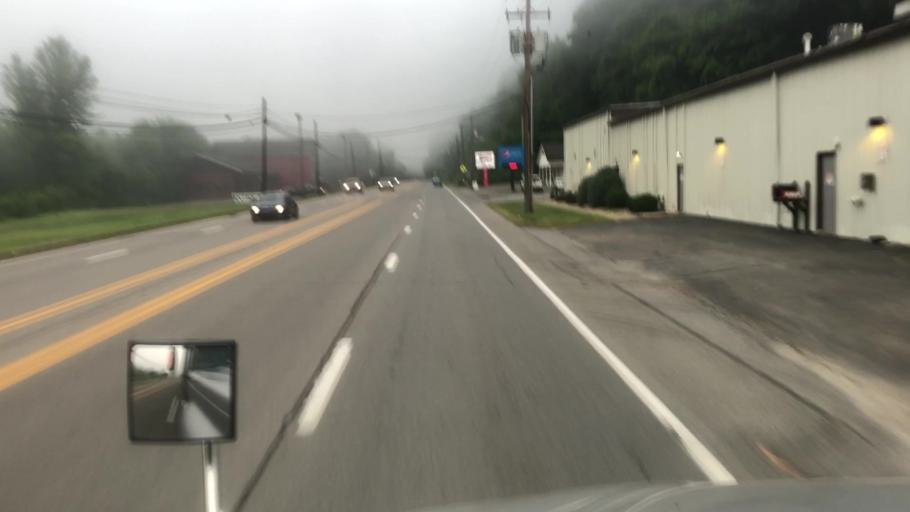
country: US
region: Pennsylvania
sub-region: Venango County
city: Franklin
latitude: 41.3994
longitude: -79.8156
